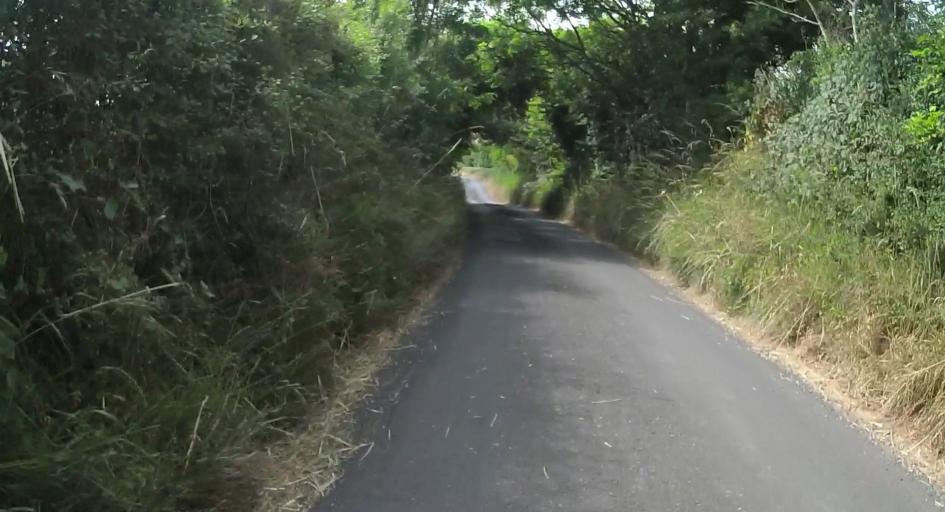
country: GB
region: England
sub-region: Dorset
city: Swanage
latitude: 50.6348
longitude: -2.0310
